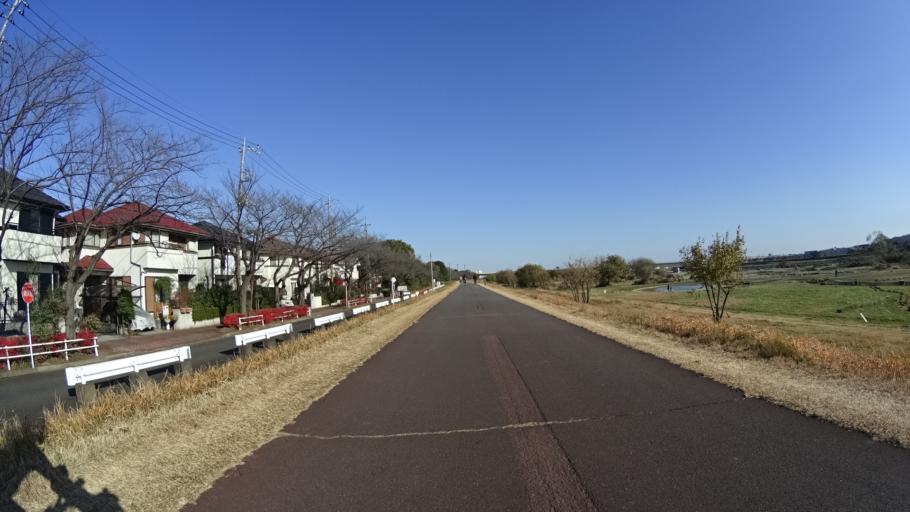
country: JP
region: Tokyo
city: Chofugaoka
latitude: 35.6535
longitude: 139.5045
